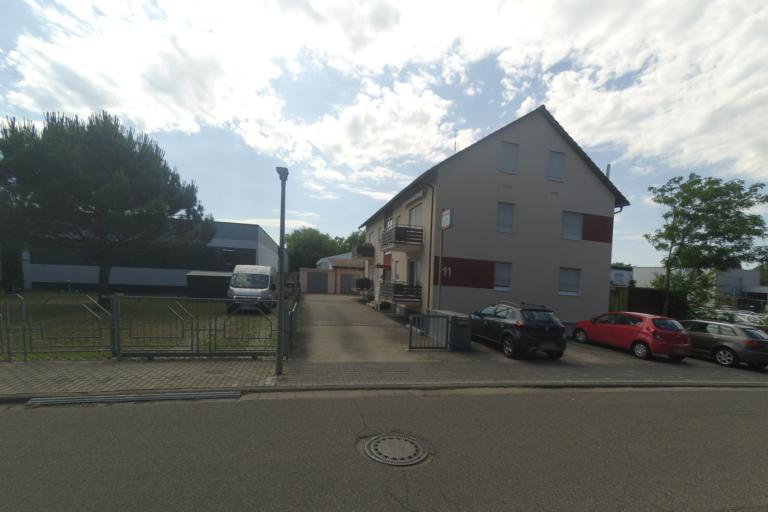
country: DE
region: Rheinland-Pfalz
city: Neuhofen
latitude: 49.4253
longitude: 8.4144
